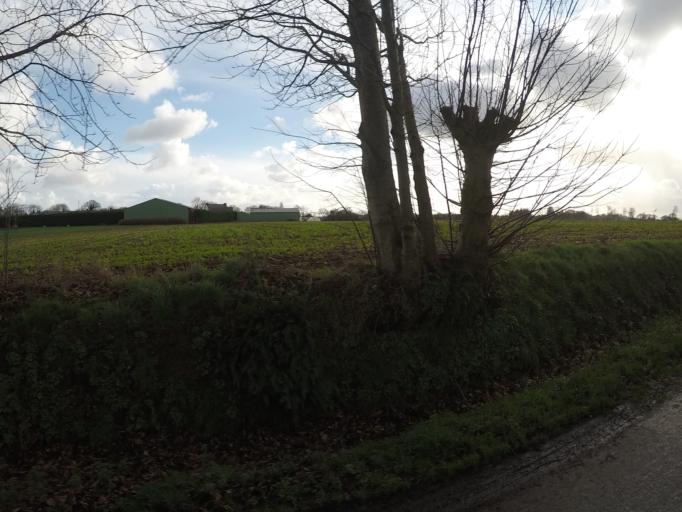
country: FR
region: Brittany
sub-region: Departement des Cotes-d'Armor
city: Lanvollon
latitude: 48.6120
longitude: -2.9942
